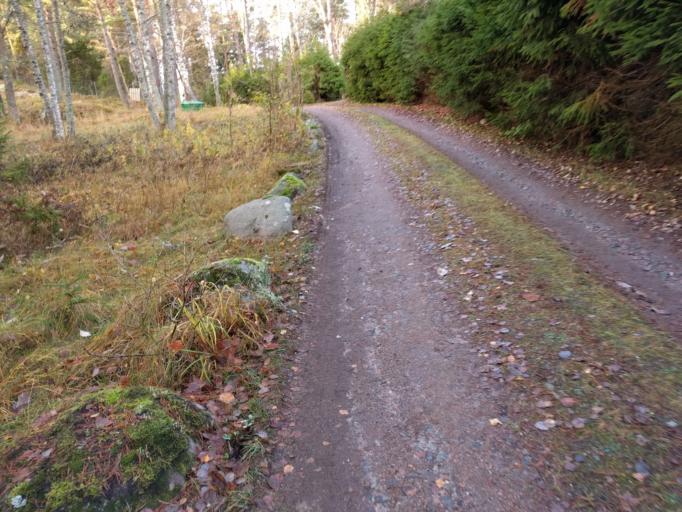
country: SE
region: Stockholm
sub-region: Osterakers Kommun
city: Akersberga
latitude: 59.5961
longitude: 18.3491
